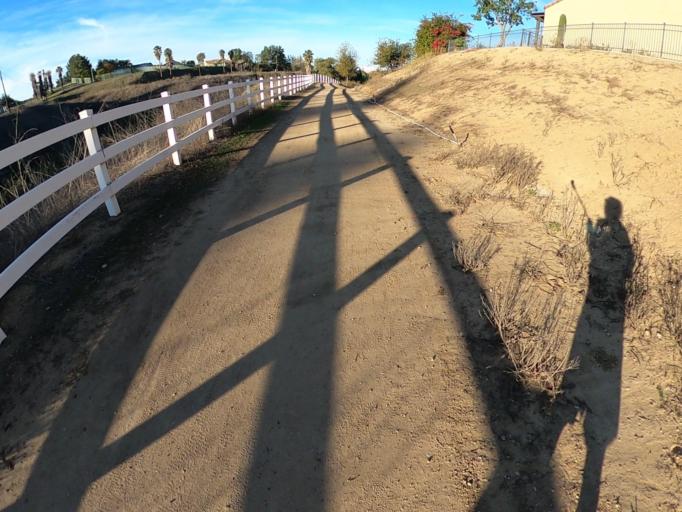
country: US
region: California
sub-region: Orange County
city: Brea
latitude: 33.8973
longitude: -117.9140
